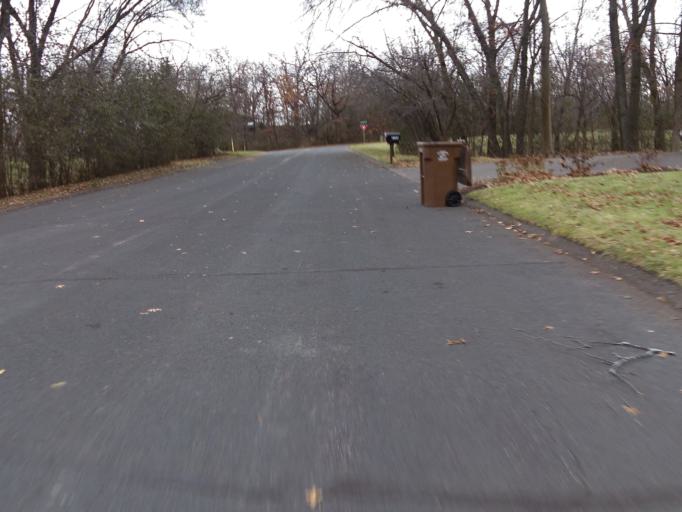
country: US
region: Minnesota
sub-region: Washington County
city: Lake Elmo
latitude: 44.9809
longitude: -92.8708
